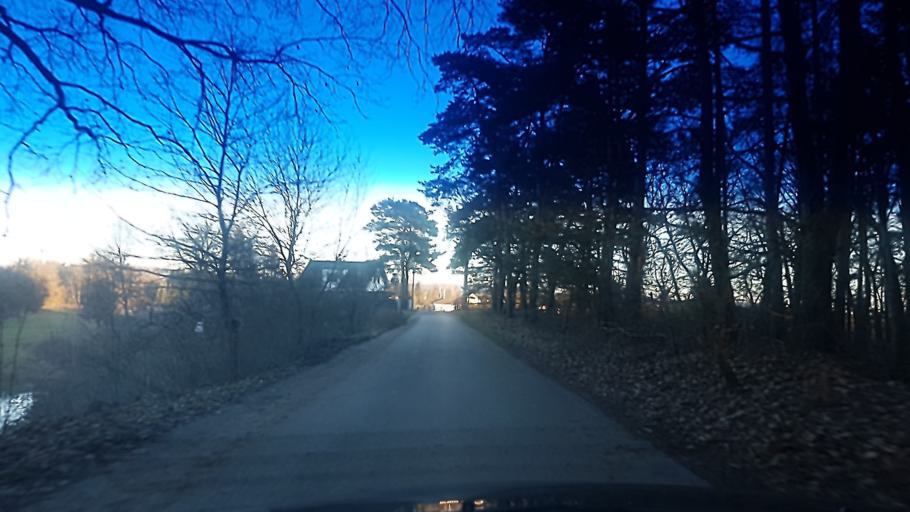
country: DE
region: Bavaria
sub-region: Upper Franconia
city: Gundelsheim
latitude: 49.9275
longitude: 10.9020
